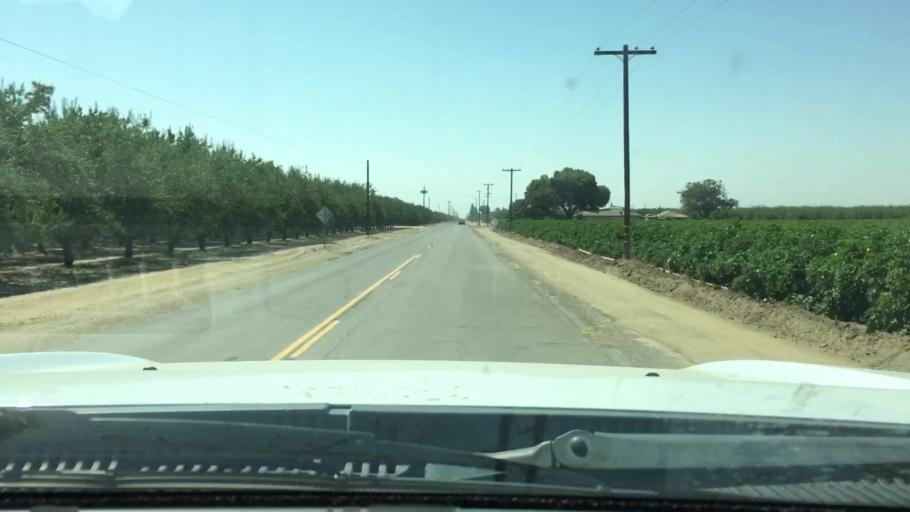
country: US
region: California
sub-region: Kern County
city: Shafter
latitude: 35.5454
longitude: -119.2776
